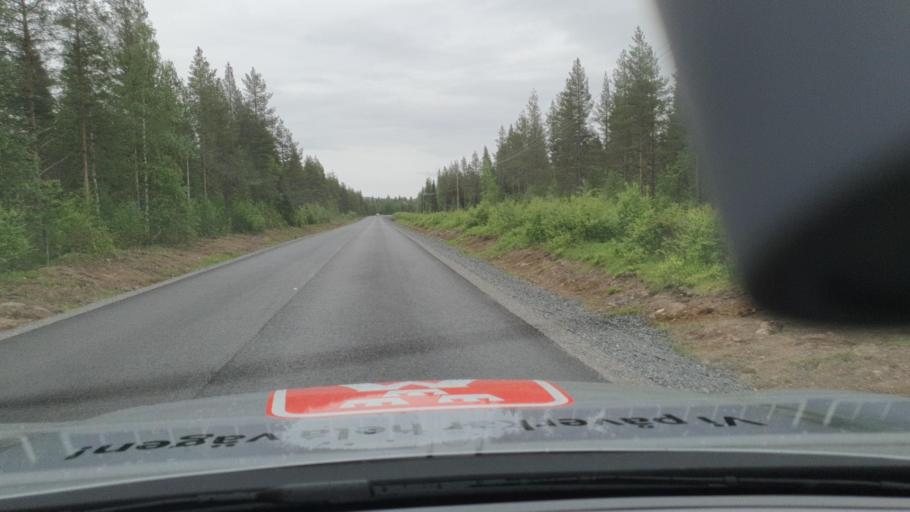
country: SE
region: Norrbotten
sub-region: Overkalix Kommun
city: OEverkalix
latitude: 66.7133
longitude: 23.1981
